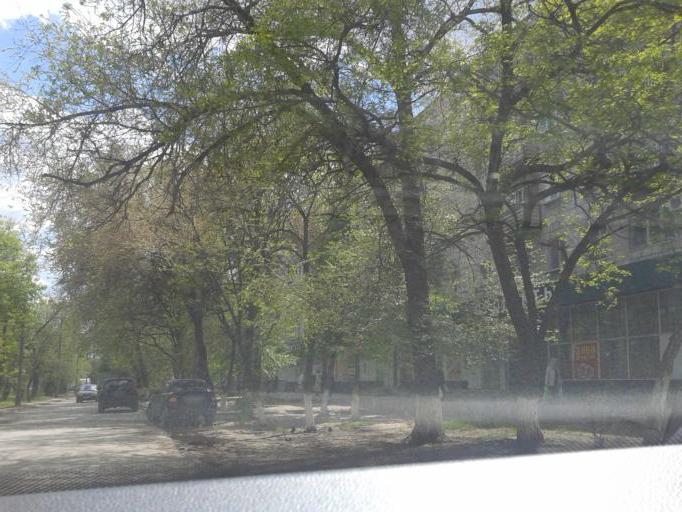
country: RU
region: Volgograd
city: Volgograd
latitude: 48.6099
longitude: 44.4217
